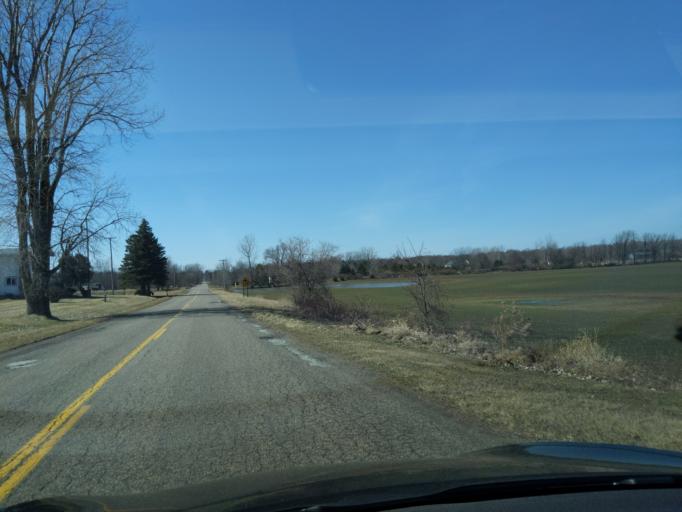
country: US
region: Michigan
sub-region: Ionia County
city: Portland
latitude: 42.7267
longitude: -84.9724
